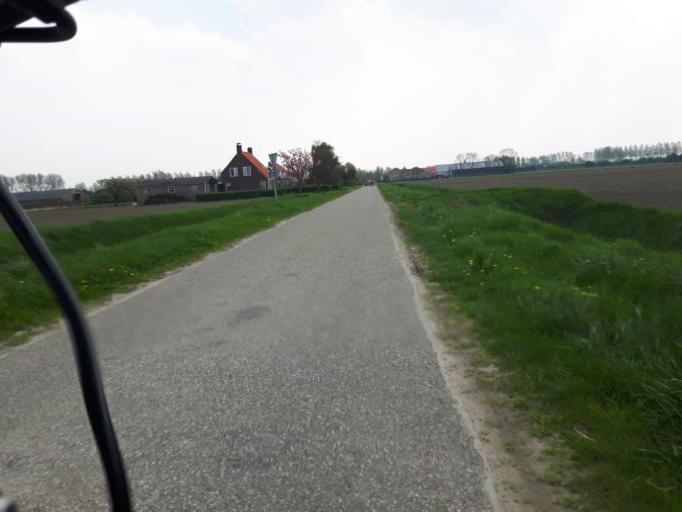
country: NL
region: Zeeland
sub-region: Gemeente Borsele
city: Borssele
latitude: 51.4620
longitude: 3.7997
